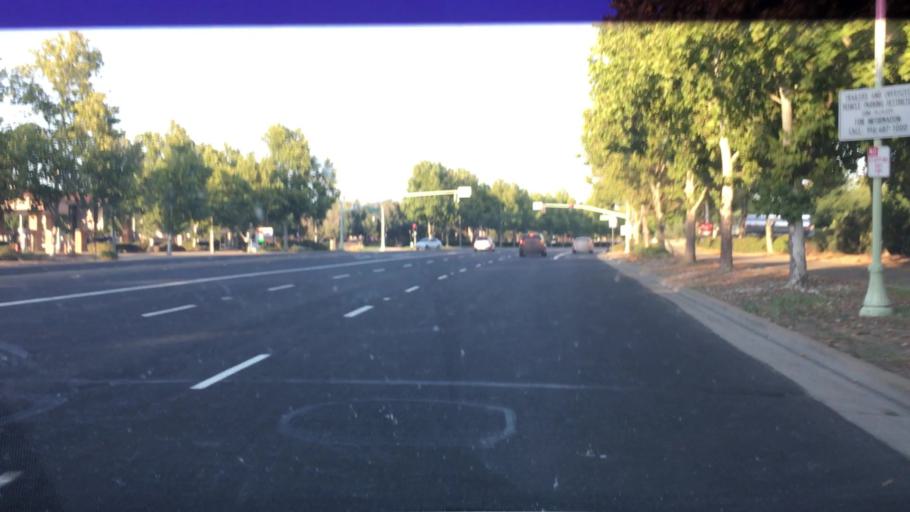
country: US
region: California
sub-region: Sacramento County
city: Laguna
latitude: 38.4273
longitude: -121.4821
